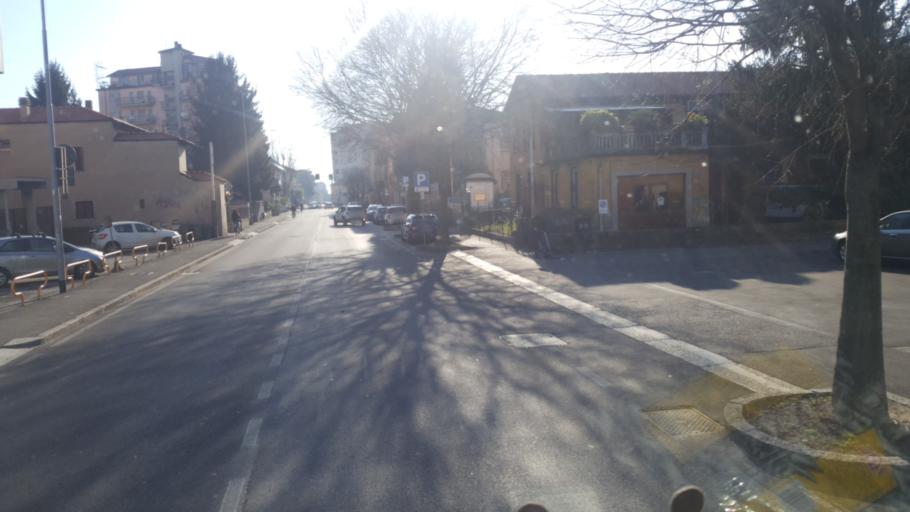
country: IT
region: Lombardy
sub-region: Provincia di Bergamo
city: Bergamo
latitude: 45.6807
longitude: 9.6616
